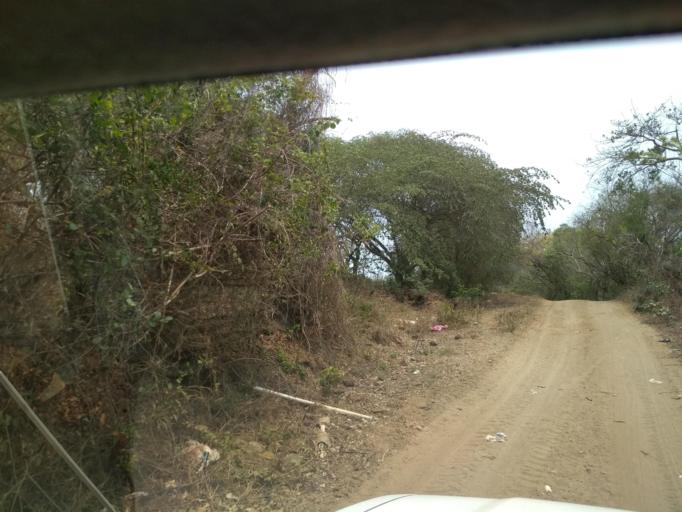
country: MX
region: Veracruz
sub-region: Veracruz
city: Delfino Victoria (Santa Fe)
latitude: 19.2120
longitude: -96.2672
